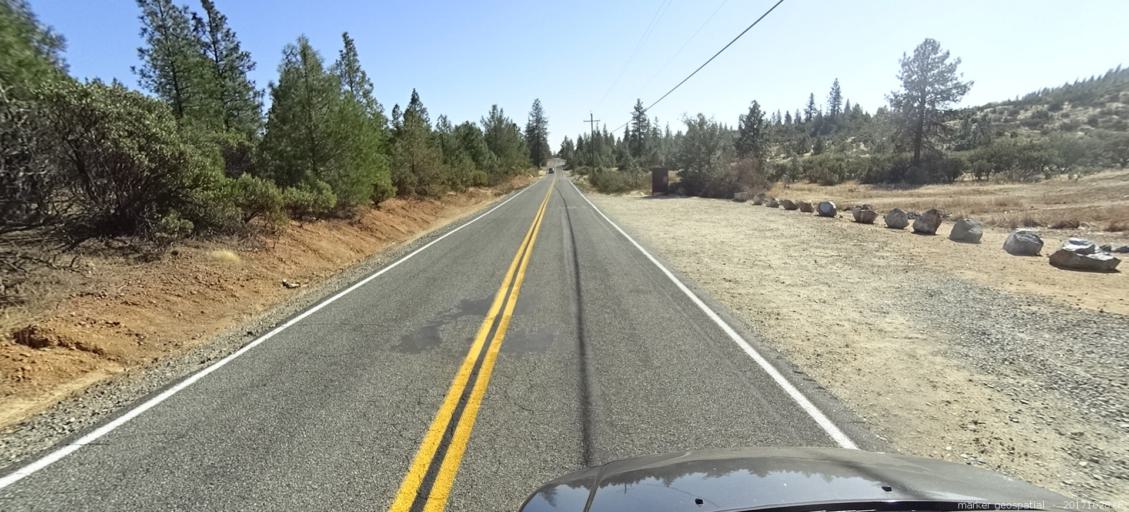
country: US
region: California
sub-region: Shasta County
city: Shasta
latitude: 40.6455
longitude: -122.4586
